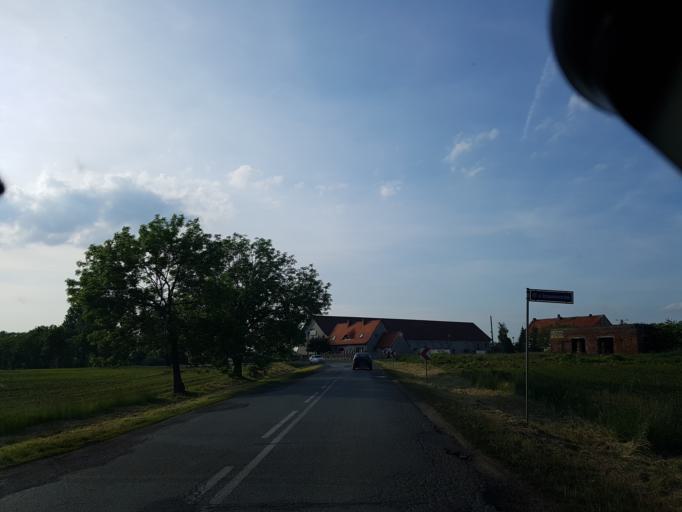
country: PL
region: Lower Silesian Voivodeship
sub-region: Powiat wroclawski
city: Kobierzyce
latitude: 50.9474
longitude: 16.9192
